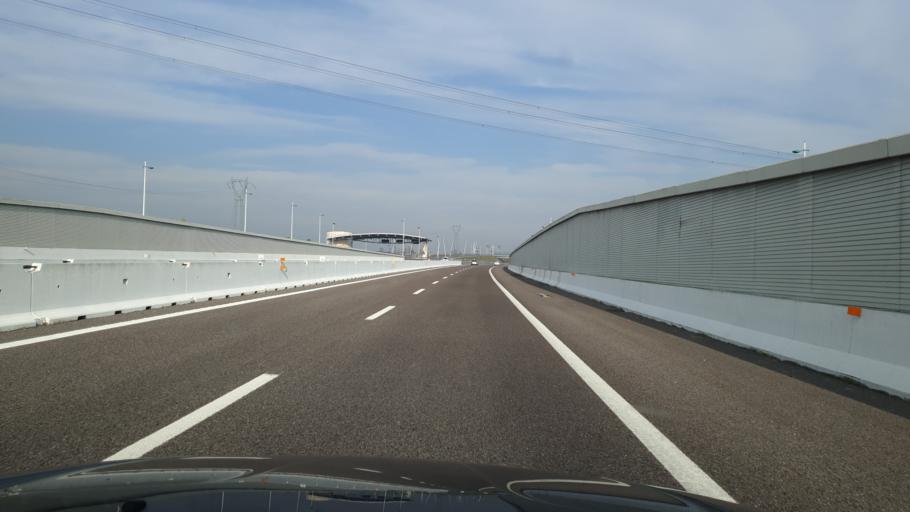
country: IT
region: Veneto
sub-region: Provincia di Vicenza
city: Ponte di Barbarano
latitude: 45.3817
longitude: 11.6120
